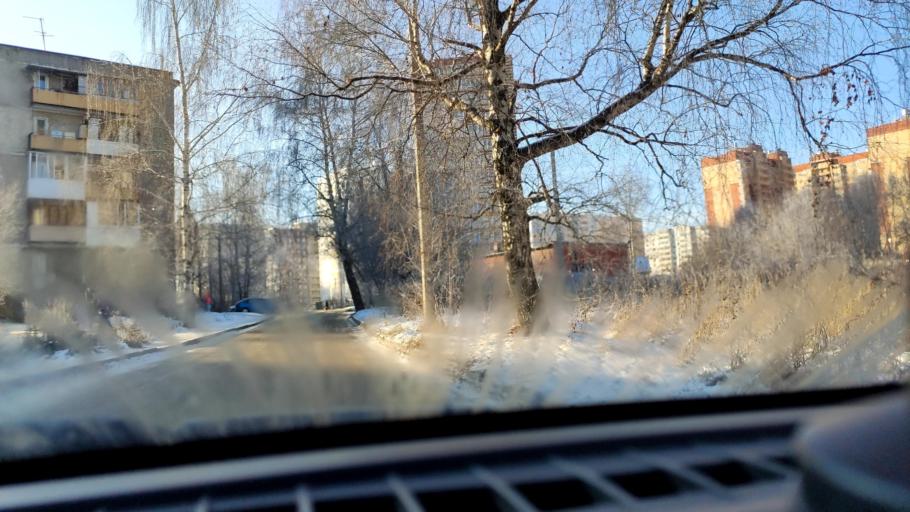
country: RU
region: Perm
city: Kondratovo
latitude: 58.0301
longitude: 56.0247
